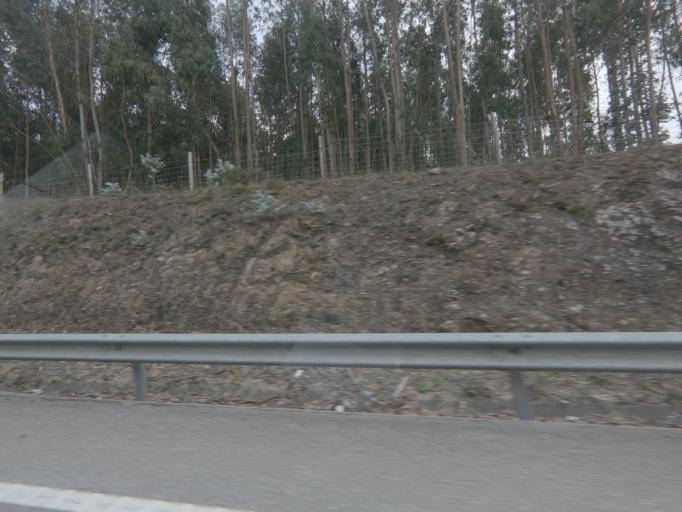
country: PT
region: Coimbra
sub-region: Penacova
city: Lorvao
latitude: 40.3034
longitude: -8.3472
